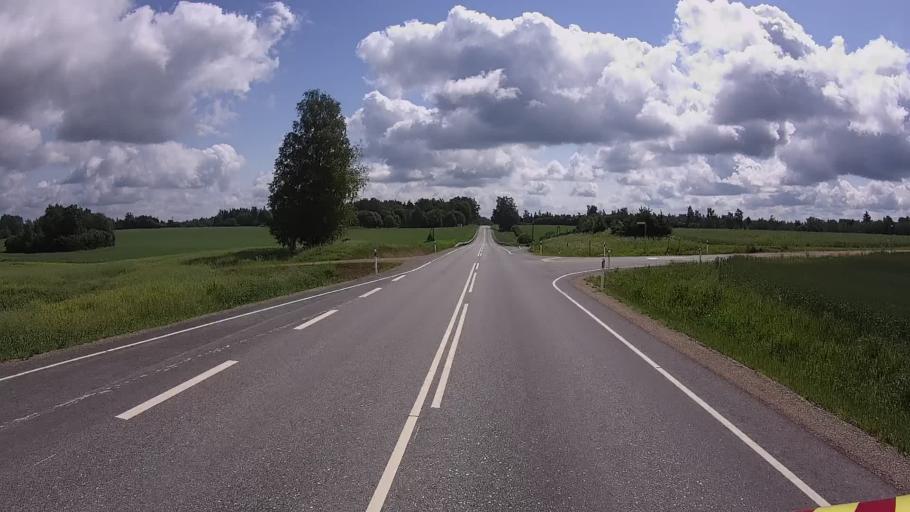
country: EE
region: Viljandimaa
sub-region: Viiratsi vald
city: Viiratsi
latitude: 58.3362
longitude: 25.6362
